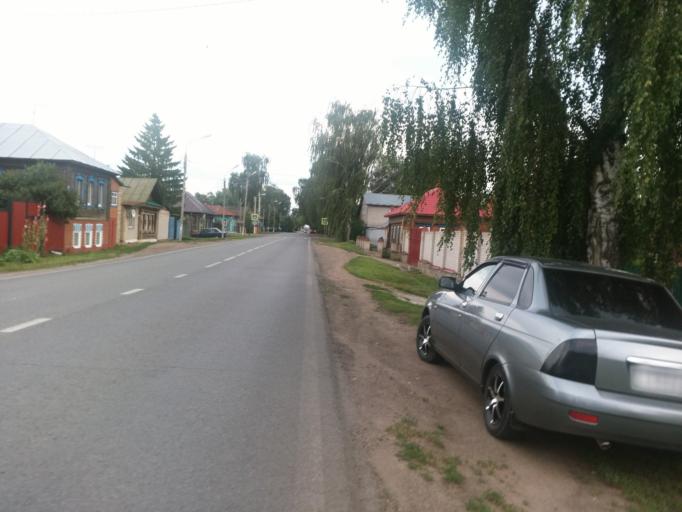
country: RU
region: Tatarstan
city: Yelabuga
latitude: 55.7559
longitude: 52.0743
